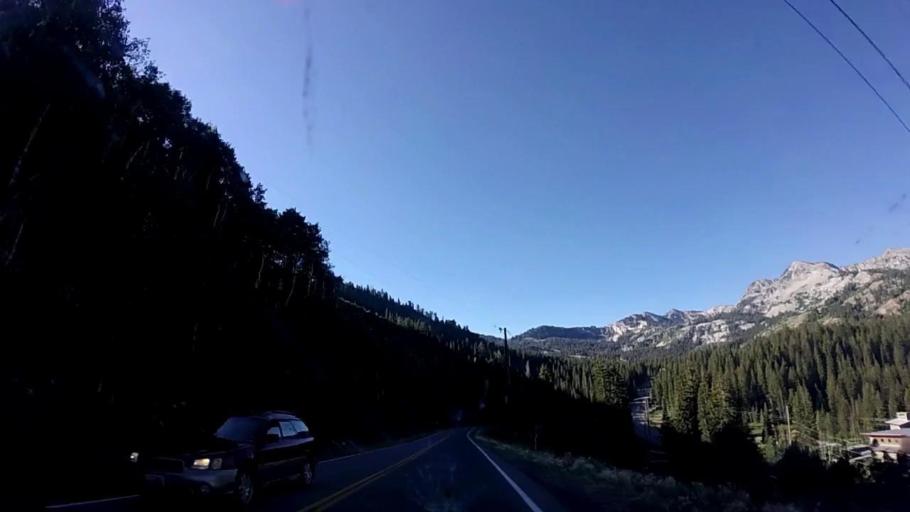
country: US
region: Utah
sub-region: Summit County
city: Park City
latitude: 40.6112
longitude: -111.5791
